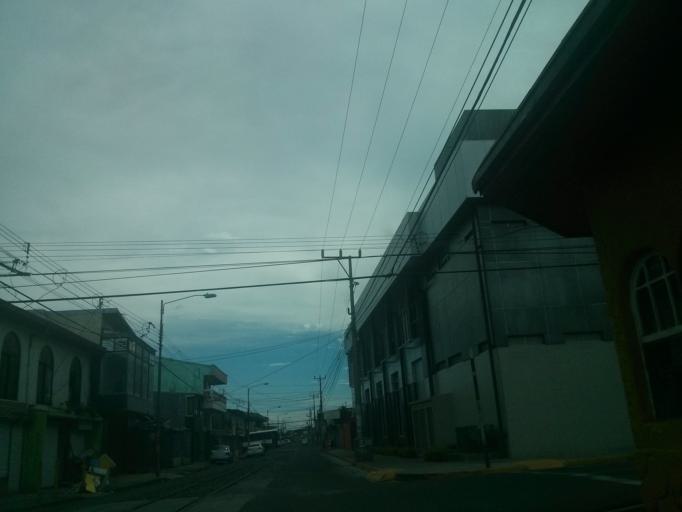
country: CR
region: Heredia
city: Heredia
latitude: 9.9950
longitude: -84.1200
